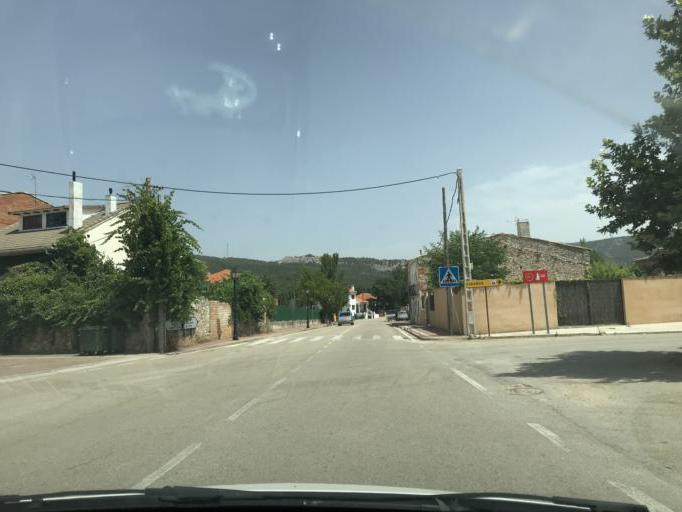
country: ES
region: Castille-La Mancha
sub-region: Provincia de Cuenca
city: Canamares
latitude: 40.4518
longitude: -2.2379
